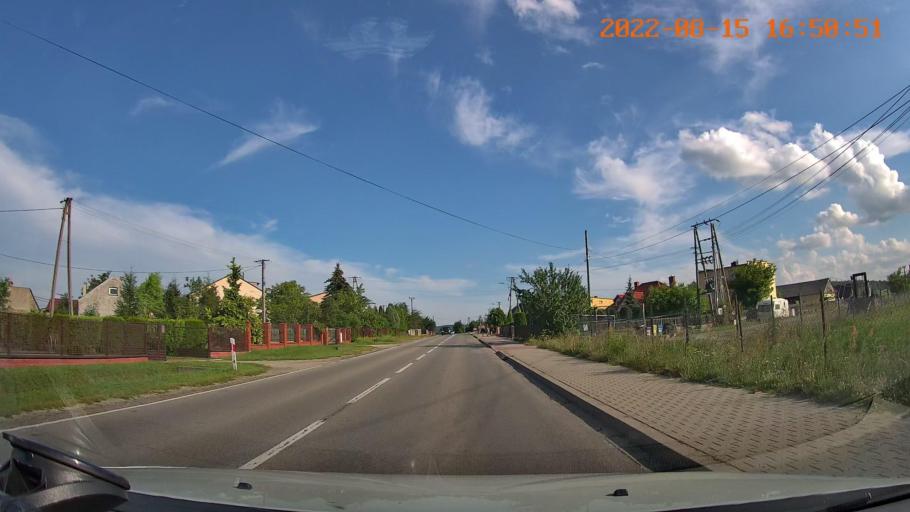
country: PL
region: Swietokrzyskie
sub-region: Powiat kielecki
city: Piekoszow
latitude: 50.8706
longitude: 20.4741
